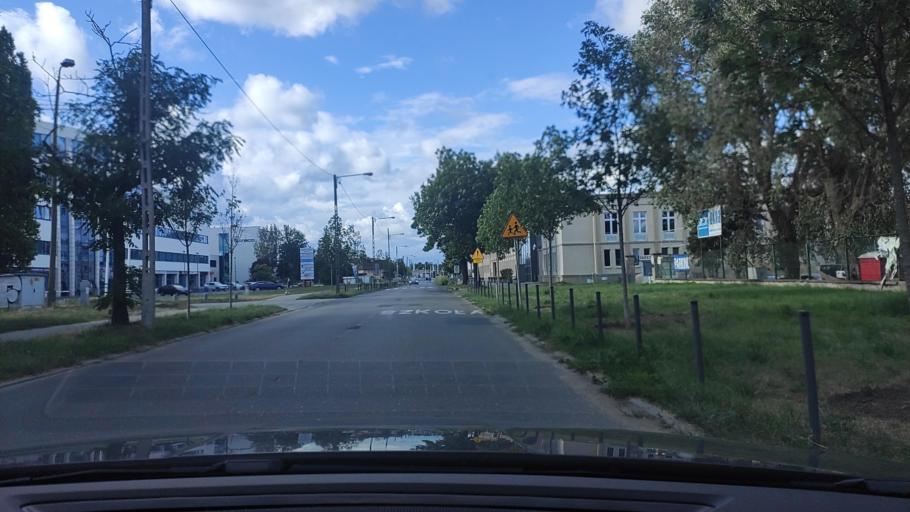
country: PL
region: Greater Poland Voivodeship
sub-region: Poznan
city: Poznan
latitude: 52.4134
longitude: 16.9651
